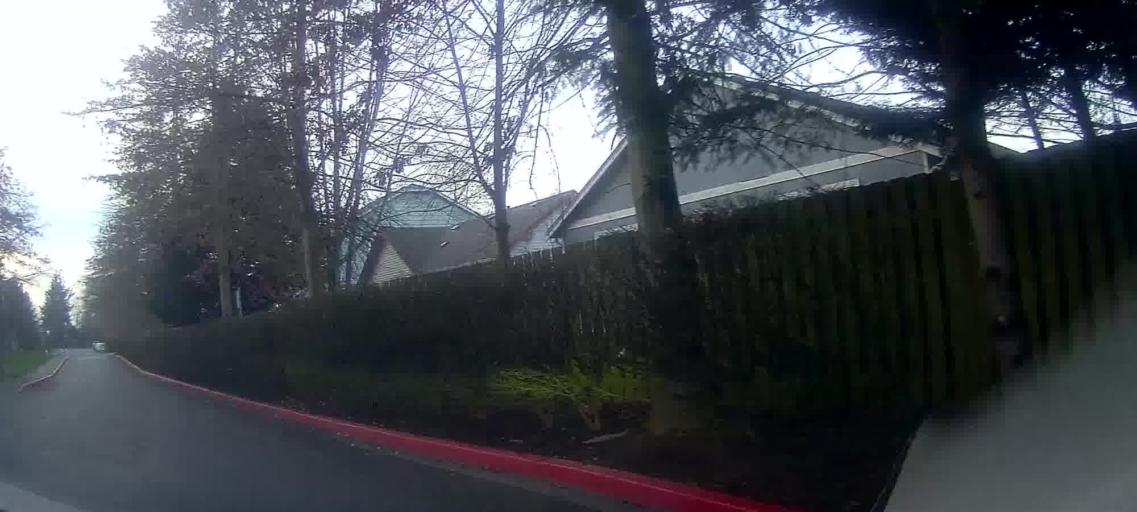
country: US
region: Washington
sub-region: Skagit County
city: Mount Vernon
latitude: 48.4402
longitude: -122.3272
